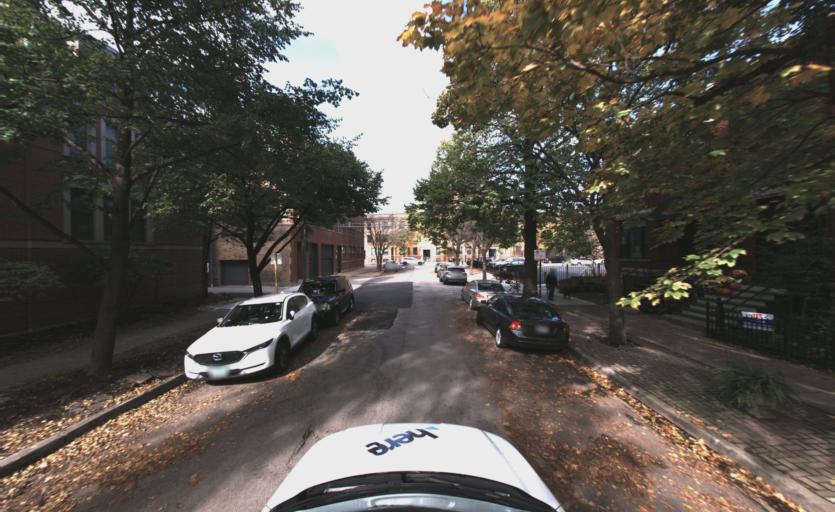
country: US
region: Illinois
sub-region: Cook County
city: Chicago
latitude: 41.9175
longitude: -87.6554
